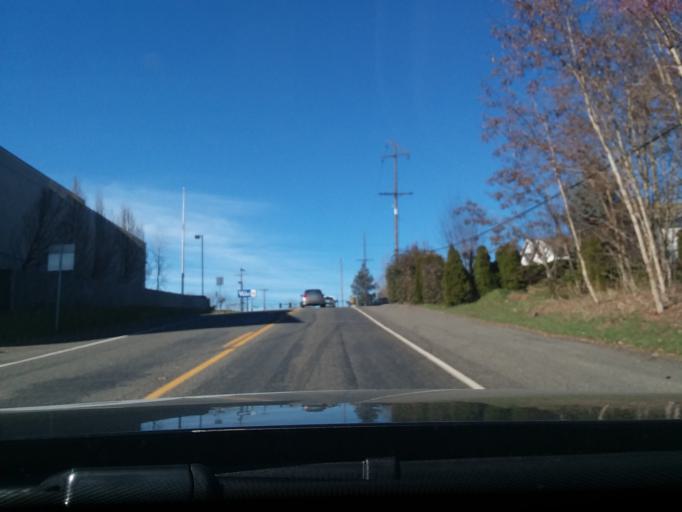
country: US
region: Washington
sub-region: Pierce County
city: Summit
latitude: 47.1616
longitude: -122.3551
